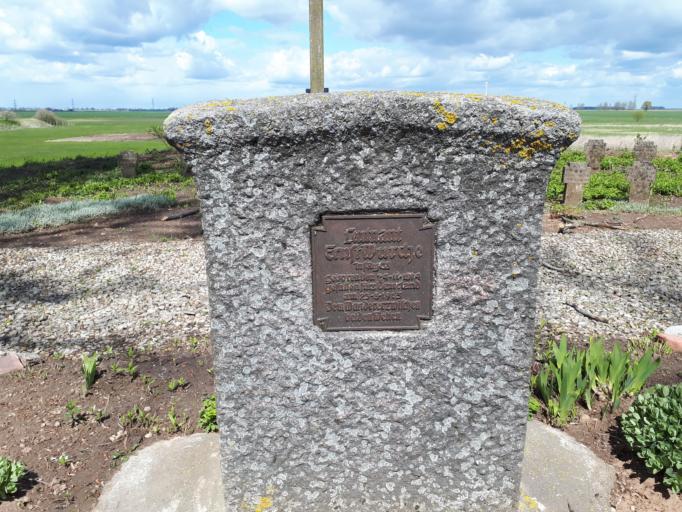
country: LT
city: Simnas
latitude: 54.3897
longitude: 23.6864
